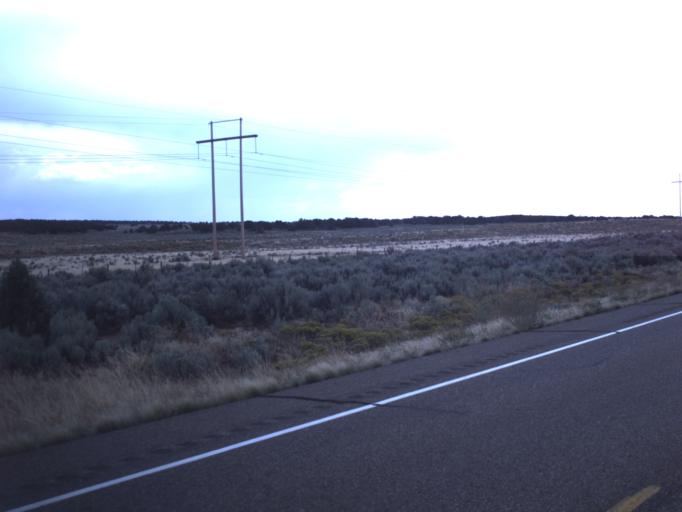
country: US
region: Utah
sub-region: Kane County
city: Kanab
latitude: 37.1691
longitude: -112.0281
